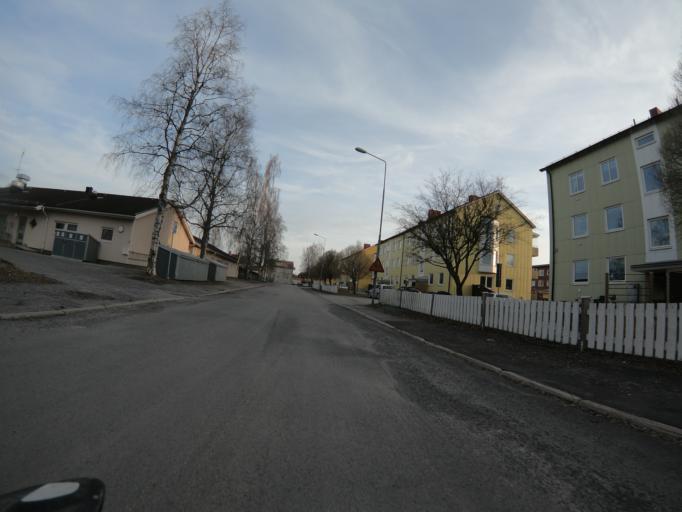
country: SE
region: Vaesterbotten
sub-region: Umea Kommun
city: Umea
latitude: 63.8337
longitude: 20.2711
